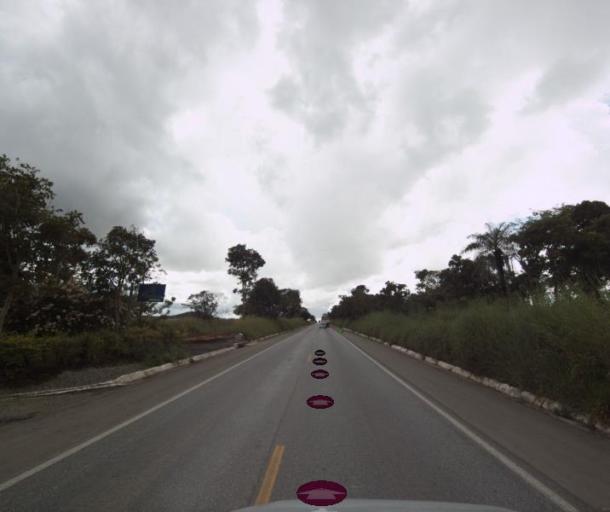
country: BR
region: Goias
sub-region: Uruacu
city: Uruacu
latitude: -14.2391
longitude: -49.1363
